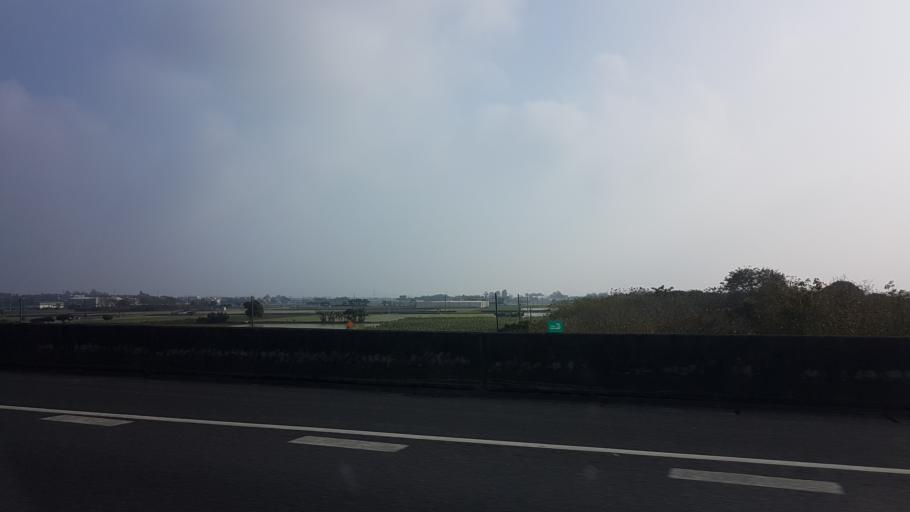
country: TW
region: Taiwan
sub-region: Chiayi
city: Taibao
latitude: 23.4229
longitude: 120.3640
